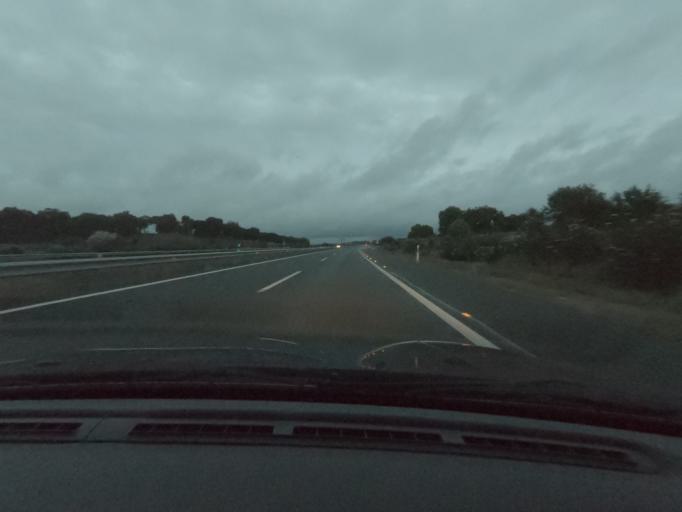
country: ES
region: Extremadura
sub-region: Provincia de Caceres
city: Casas de Don Antonio
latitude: 39.2310
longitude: -6.3024
